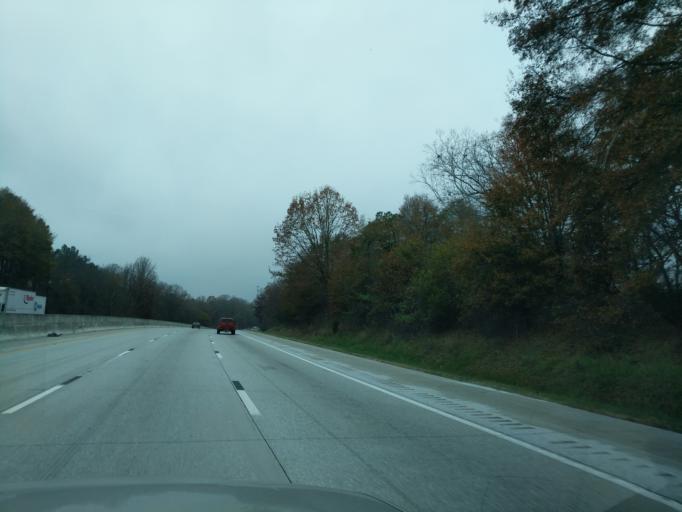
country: US
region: South Carolina
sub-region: Anderson County
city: Northlake
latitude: 34.6160
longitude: -82.6229
